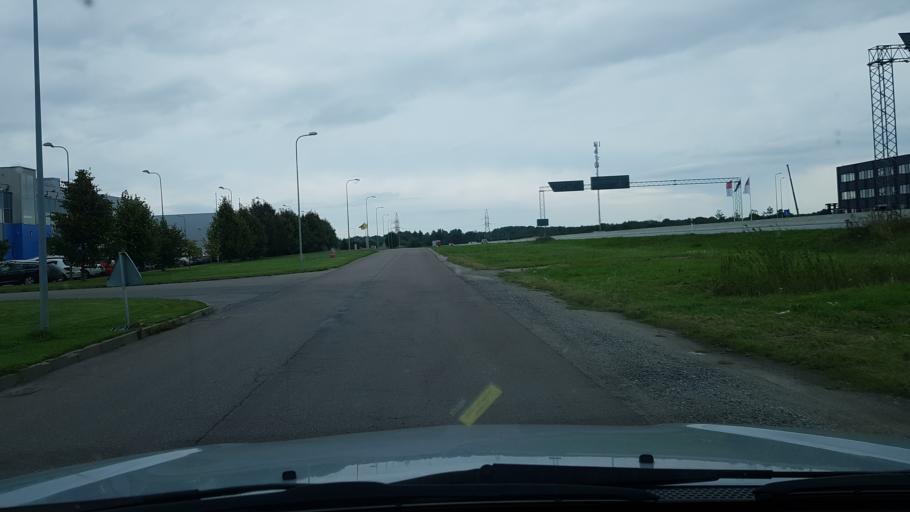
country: EE
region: Harju
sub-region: Rae vald
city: Jueri
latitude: 59.3604
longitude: 24.8943
